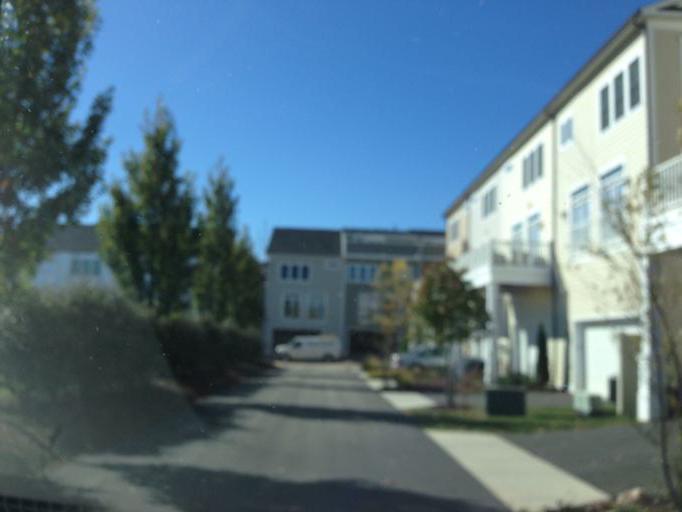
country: US
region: Maryland
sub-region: Howard County
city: Fulton
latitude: 39.1521
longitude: -76.9055
